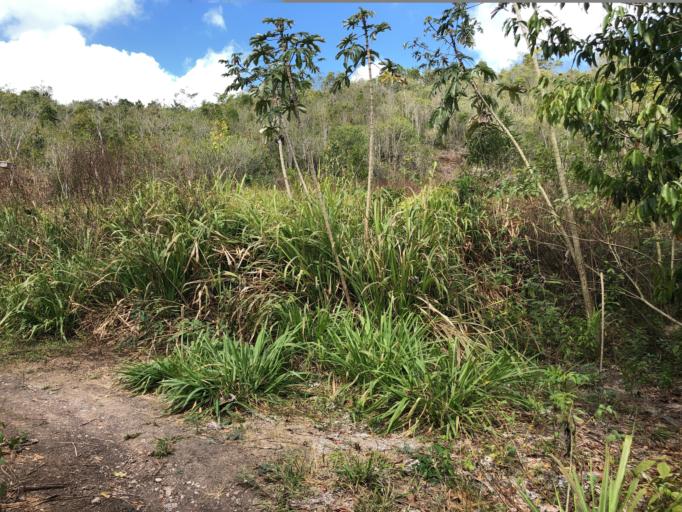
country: MX
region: Quintana Roo
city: Nicolas Bravo
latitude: 18.4472
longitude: -89.3101
